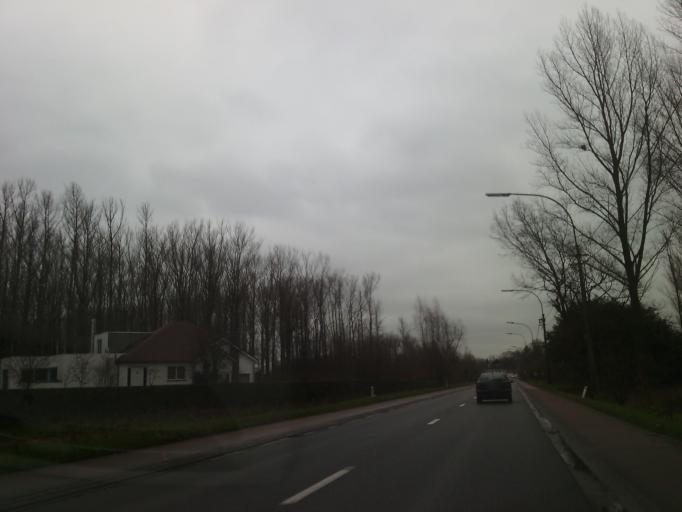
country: BE
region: Flanders
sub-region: Provincie Oost-Vlaanderen
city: Berlare
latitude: 51.0291
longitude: 3.9924
